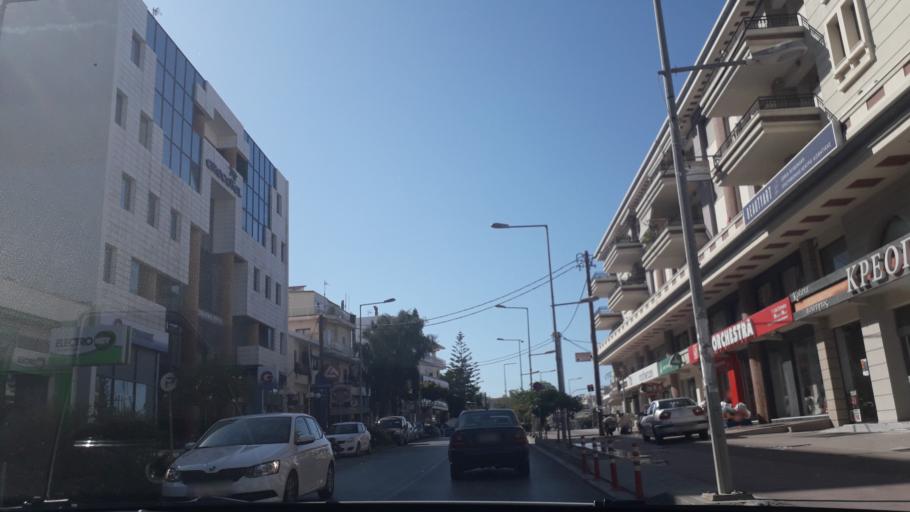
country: GR
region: Crete
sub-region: Nomos Rethymnis
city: Rethymno
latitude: 35.3644
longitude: 24.4860
